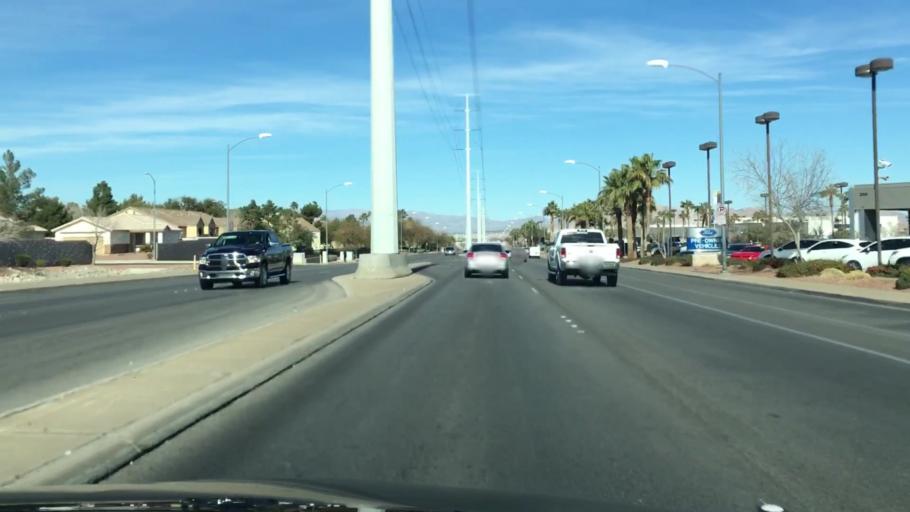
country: US
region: Nevada
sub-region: Clark County
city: Henderson
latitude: 36.0481
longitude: -115.0290
